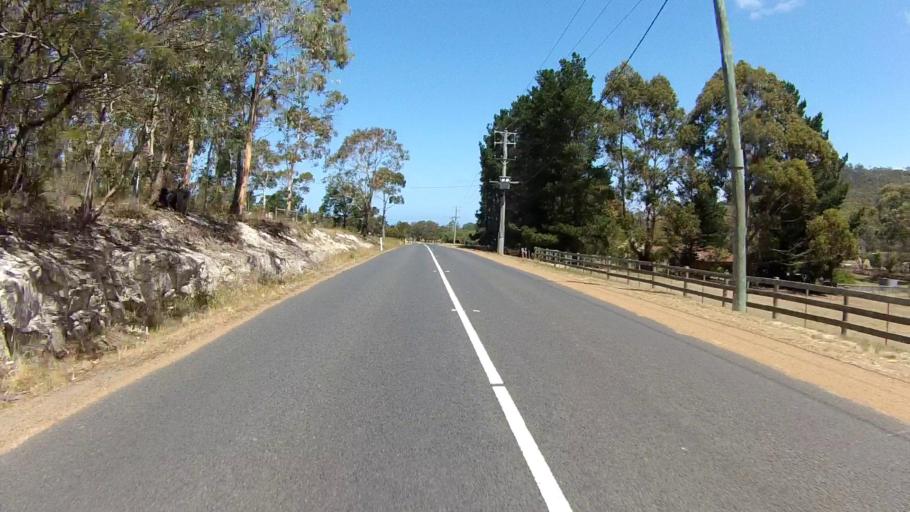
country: AU
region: Tasmania
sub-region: Clarence
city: Sandford
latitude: -42.9611
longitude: 147.4743
